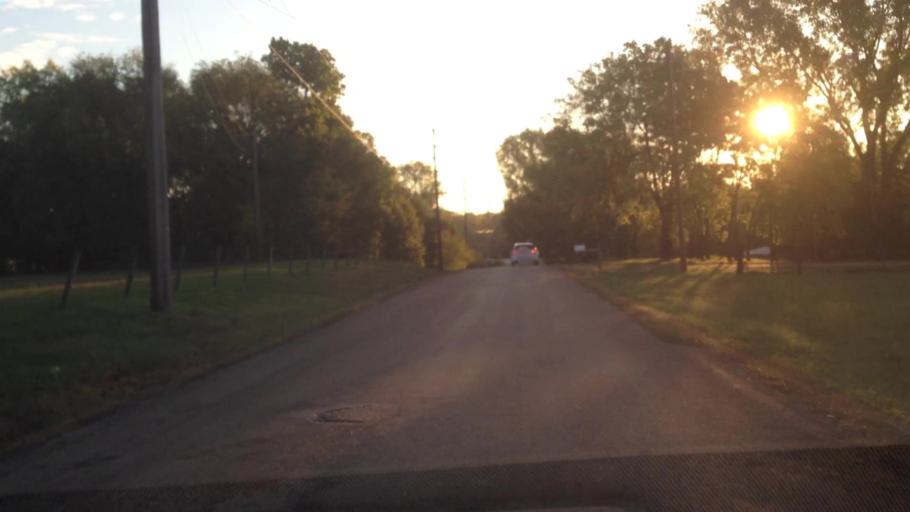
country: US
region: Kansas
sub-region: Johnson County
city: De Soto
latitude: 38.9567
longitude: -94.9894
